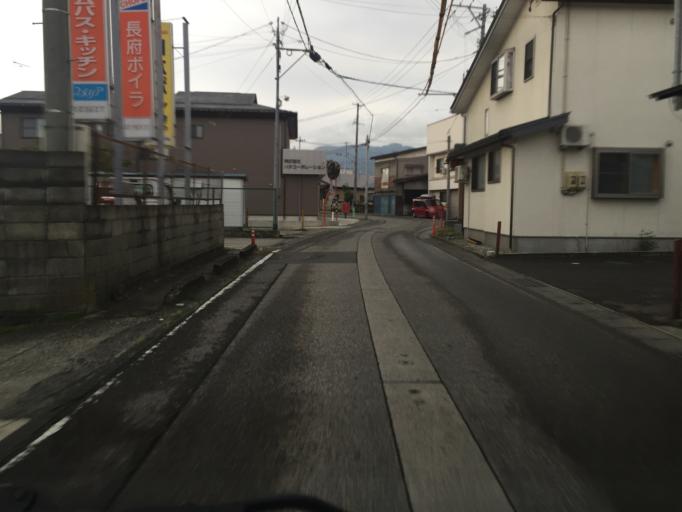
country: JP
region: Fukushima
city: Kitakata
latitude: 37.4928
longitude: 139.9099
